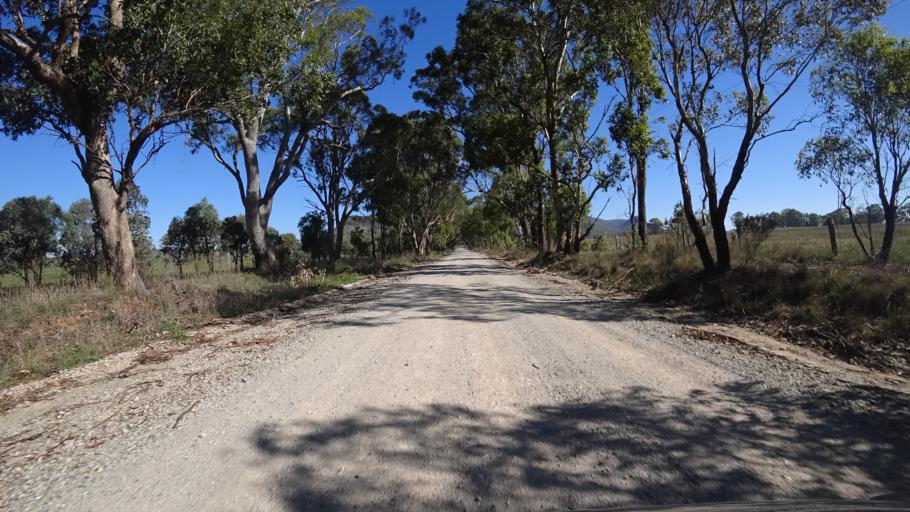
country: AU
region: New South Wales
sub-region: Mid-Western Regional
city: Kandos
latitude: -32.8299
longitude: 150.0161
